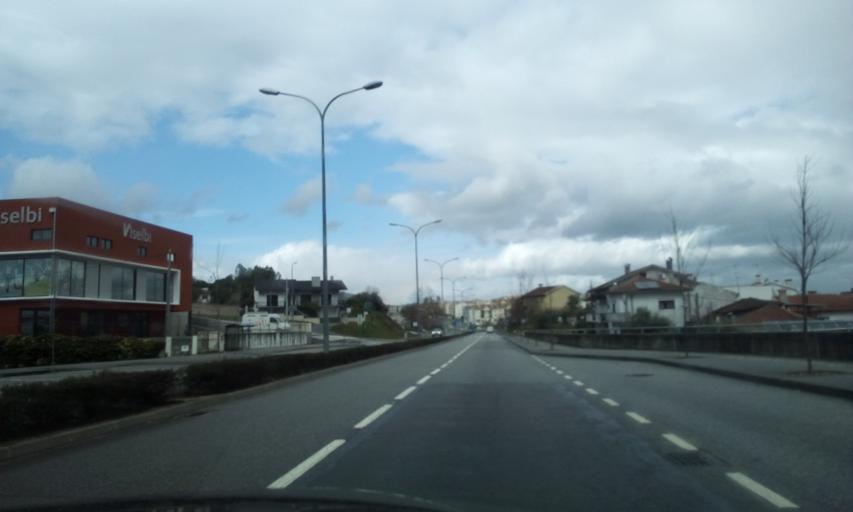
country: PT
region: Viseu
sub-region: Viseu
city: Viseu
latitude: 40.6277
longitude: -7.9141
